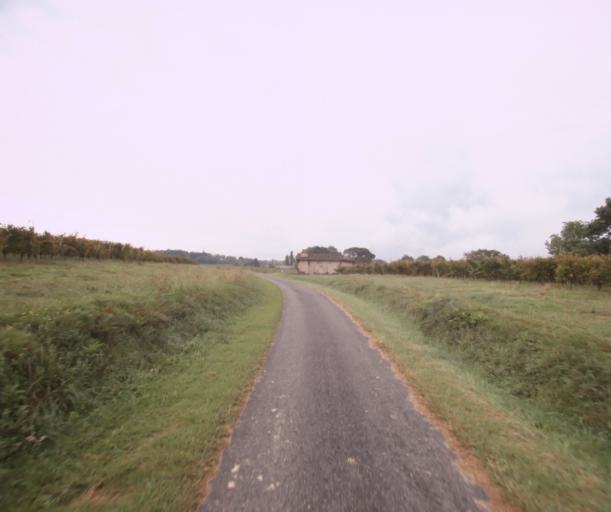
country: FR
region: Midi-Pyrenees
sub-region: Departement du Gers
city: Cazaubon
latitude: 43.9204
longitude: -0.1320
